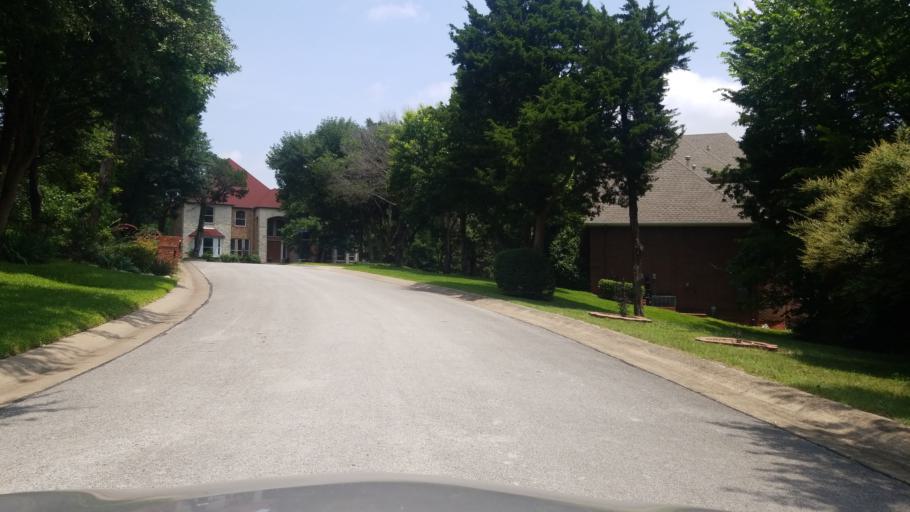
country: US
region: Texas
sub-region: Dallas County
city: Duncanville
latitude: 32.6754
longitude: -96.9176
